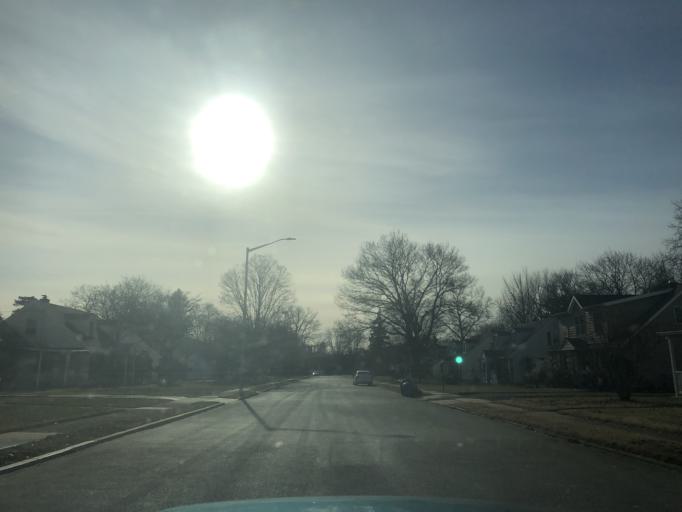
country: US
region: Pennsylvania
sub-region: Montgomery County
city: Flourtown
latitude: 40.1163
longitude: -75.1992
